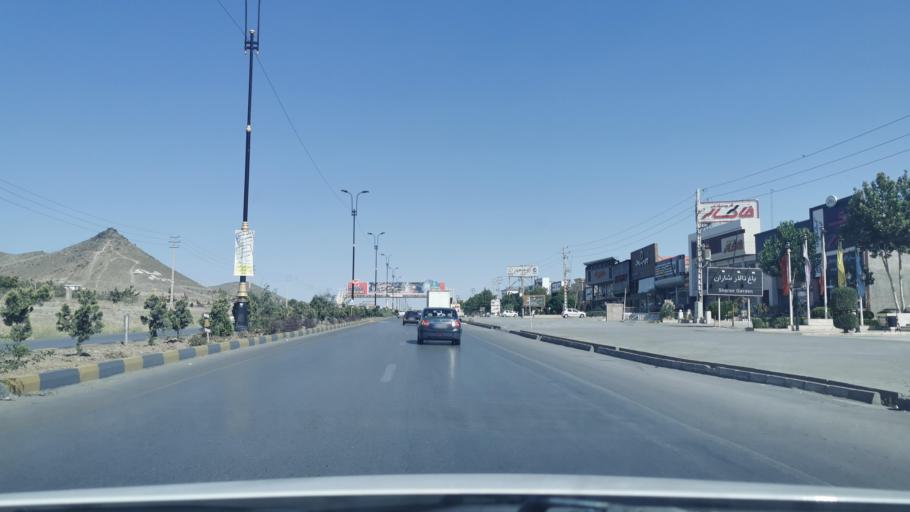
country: IR
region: Razavi Khorasan
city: Torqabeh
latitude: 36.3920
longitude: 59.4030
